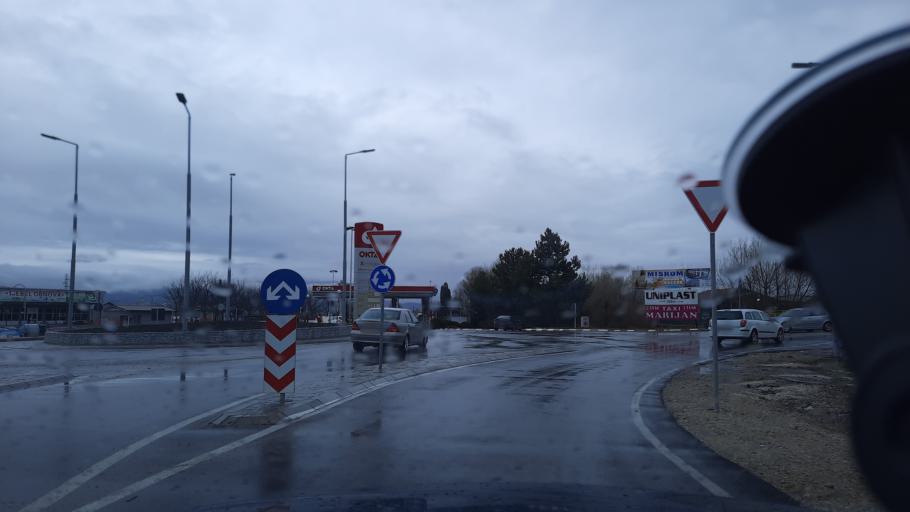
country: MK
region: Struga
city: Struga
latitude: 41.1971
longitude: 20.6763
